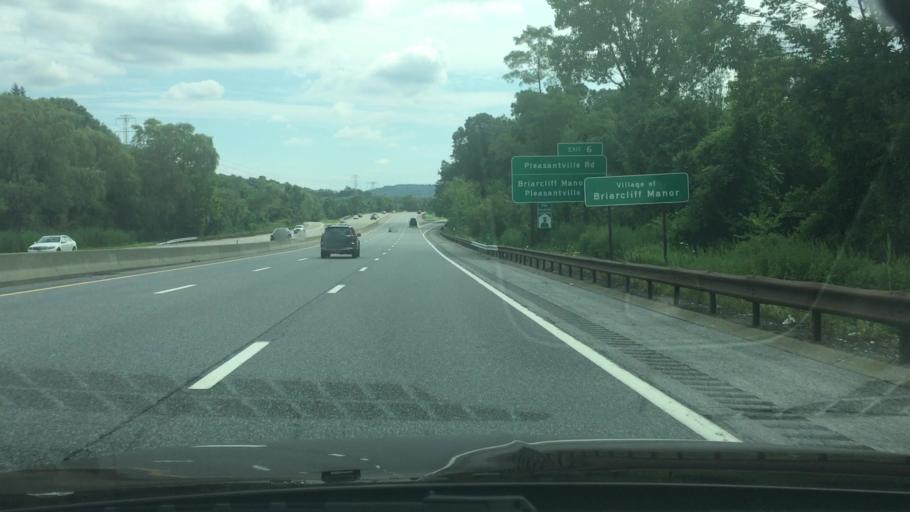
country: US
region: New York
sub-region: Westchester County
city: Briarcliff Manor
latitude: 41.1506
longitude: -73.8161
